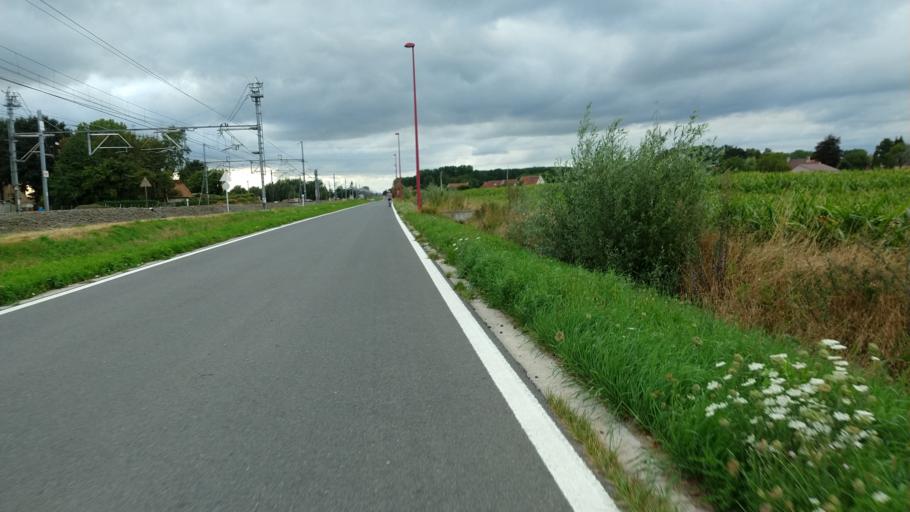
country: BE
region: Flanders
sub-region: Provincie Oost-Vlaanderen
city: Nevele
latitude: 51.0683
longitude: 3.5594
